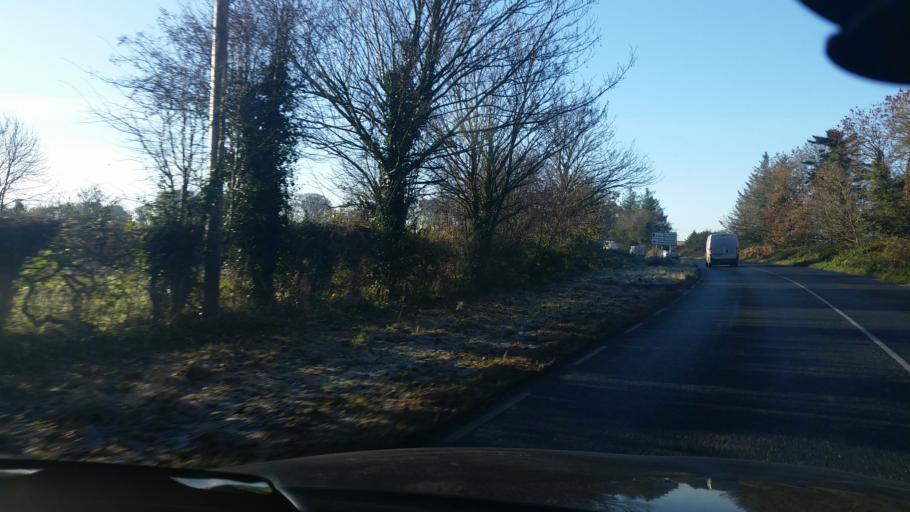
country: IE
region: Leinster
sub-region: Loch Garman
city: Ballinroad
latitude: 52.5390
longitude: -6.3461
